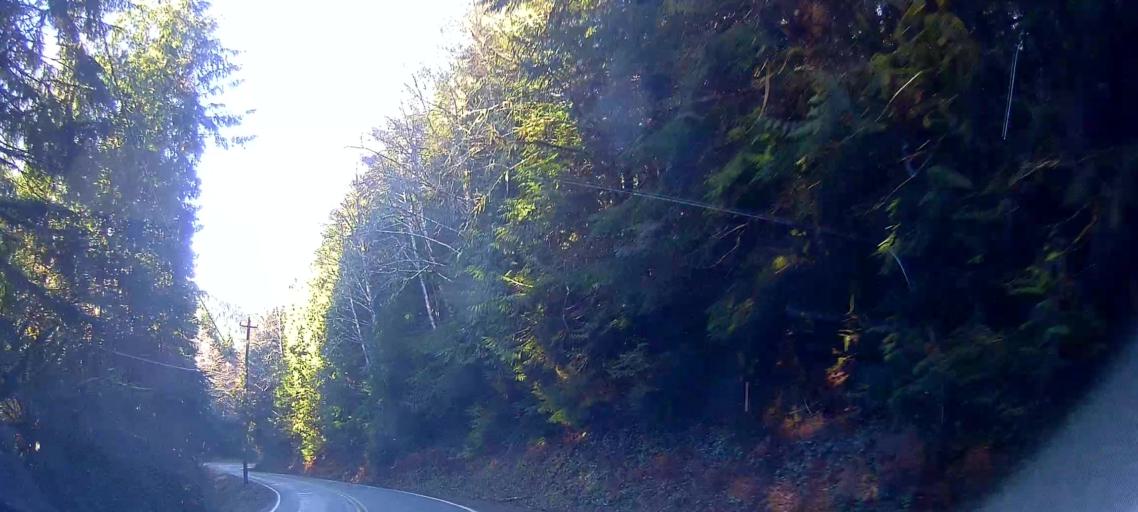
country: US
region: Washington
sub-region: Snohomish County
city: Darrington
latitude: 48.5744
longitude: -121.7736
